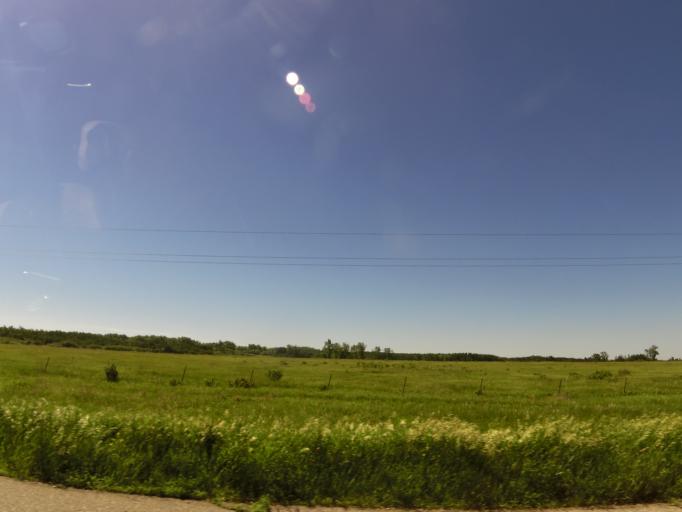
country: US
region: Minnesota
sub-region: Red Lake County
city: Red Lake Falls
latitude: 47.7604
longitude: -96.4185
